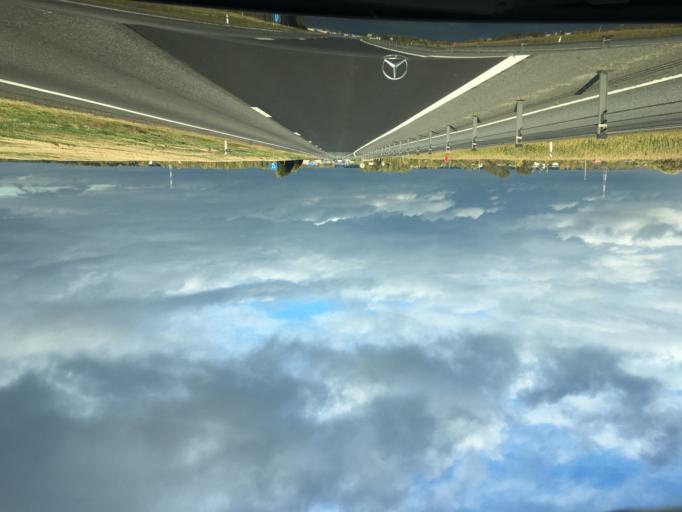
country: BY
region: Vitebsk
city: Dubrowna
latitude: 54.6542
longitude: 30.6413
